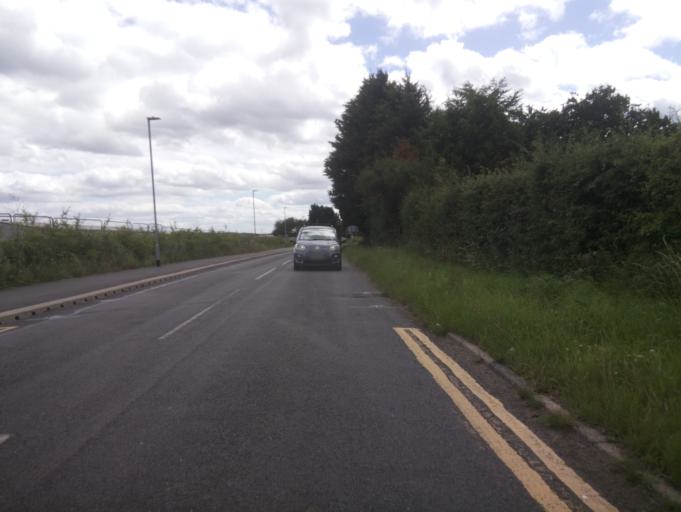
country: GB
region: England
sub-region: Nottinghamshire
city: West Bridgford
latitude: 52.9182
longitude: -1.0867
